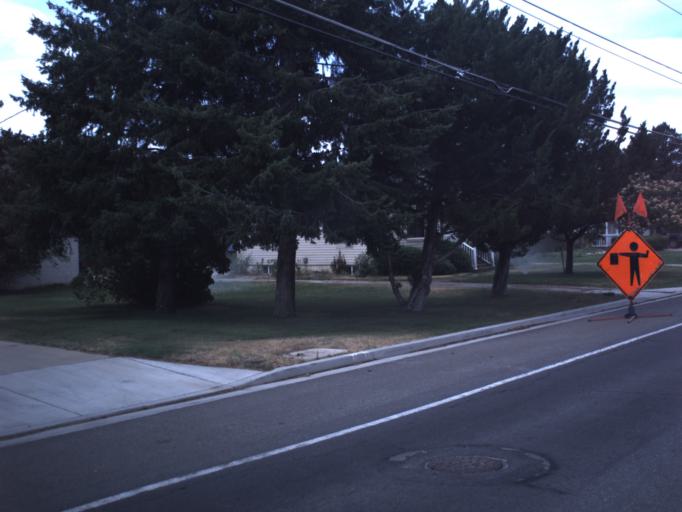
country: US
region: Utah
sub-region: Davis County
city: South Weber
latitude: 41.1345
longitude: -111.9495
